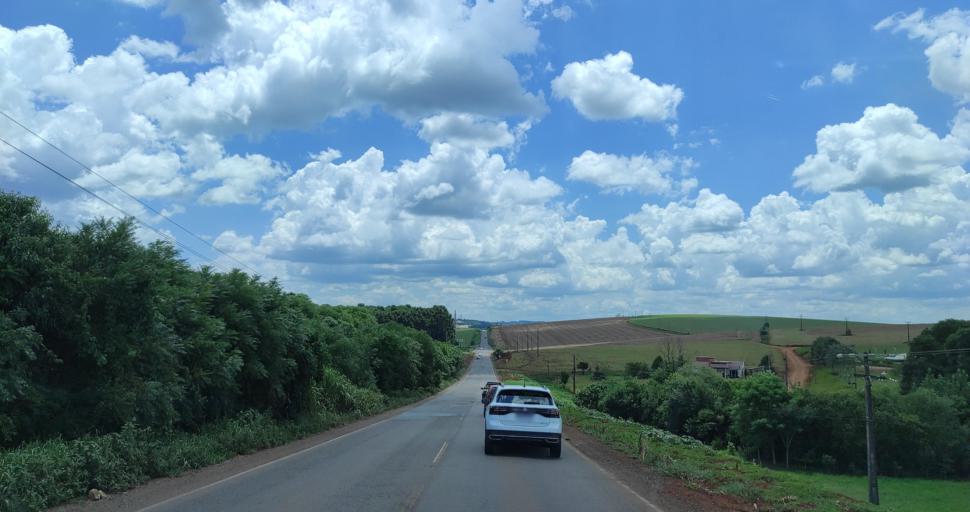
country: BR
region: Santa Catarina
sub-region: Xanxere
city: Xanxere
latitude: -26.7734
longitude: -52.4065
